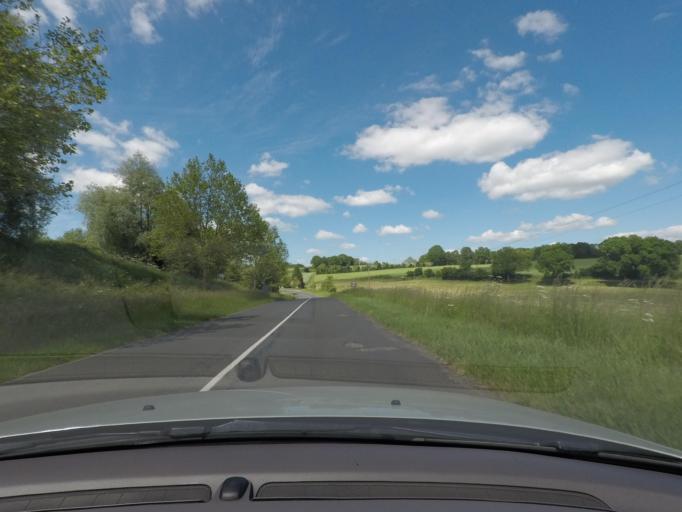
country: FR
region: Lower Normandy
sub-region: Departement de l'Orne
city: Mortagne-au-Perche
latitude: 48.5365
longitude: 0.5588
